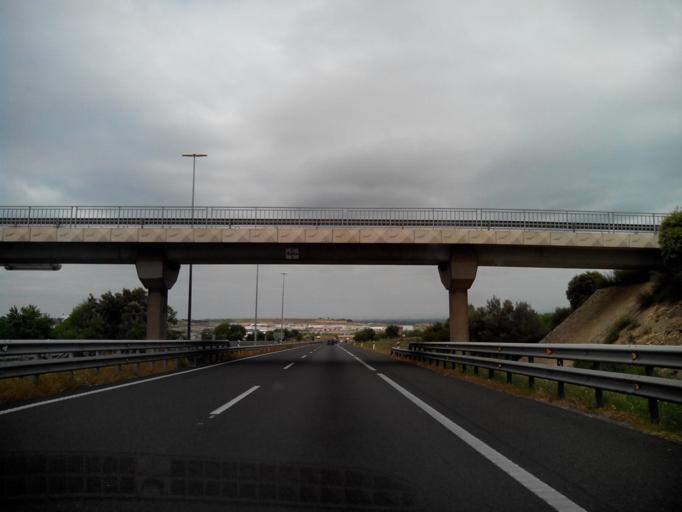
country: ES
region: Catalonia
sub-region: Provincia de Lleida
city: Tarrega
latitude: 41.6583
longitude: 1.1596
